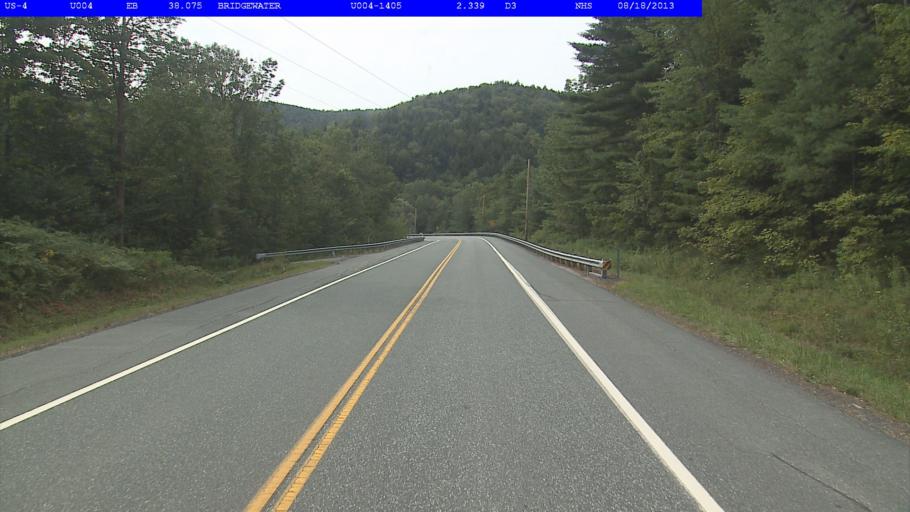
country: US
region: Vermont
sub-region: Windsor County
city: Woodstock
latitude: 43.5967
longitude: -72.7098
